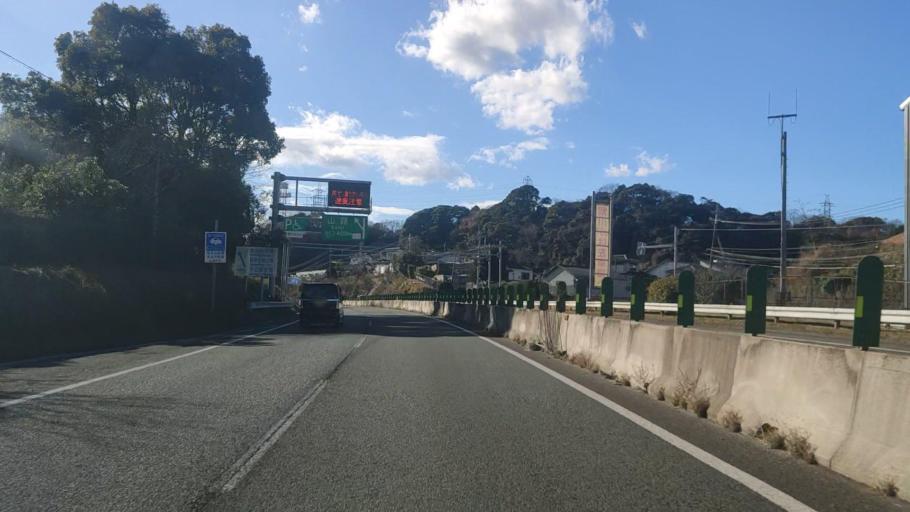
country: JP
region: Fukuoka
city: Kitakyushu
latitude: 33.8635
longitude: 130.8524
